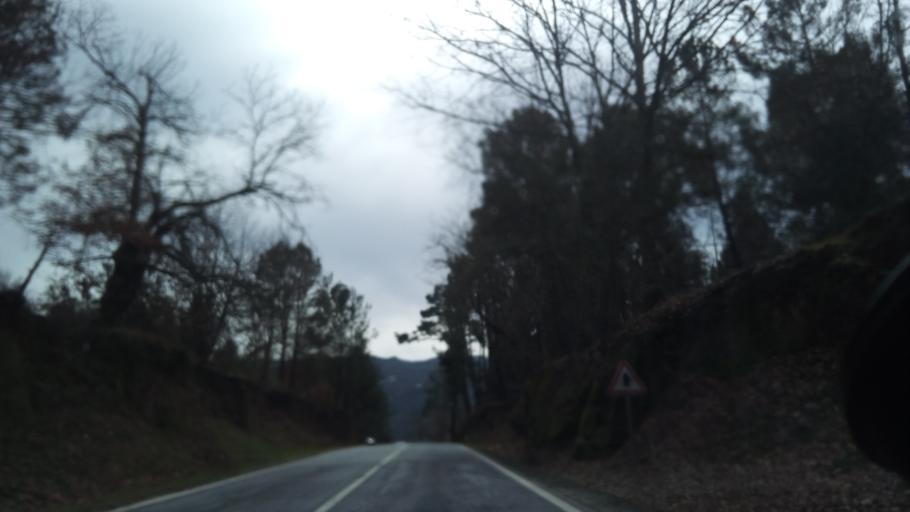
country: PT
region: Guarda
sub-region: Seia
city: Seia
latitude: 40.4431
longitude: -7.7105
